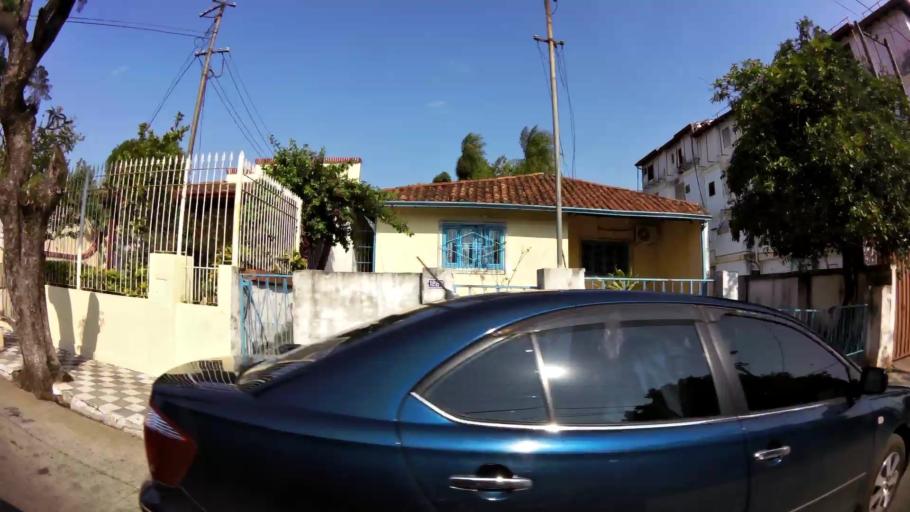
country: PY
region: Asuncion
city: Asuncion
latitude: -25.3116
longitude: -57.6260
